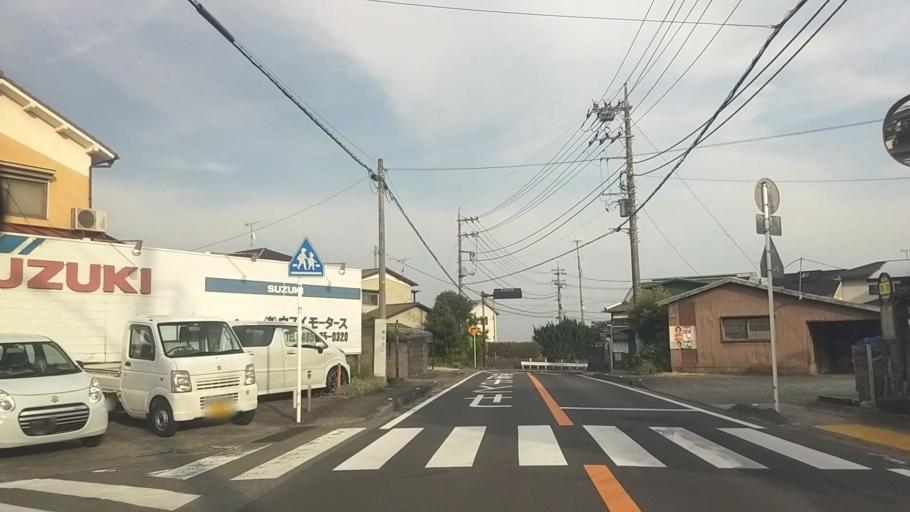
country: JP
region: Kanagawa
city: Odawara
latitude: 35.3518
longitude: 139.0937
